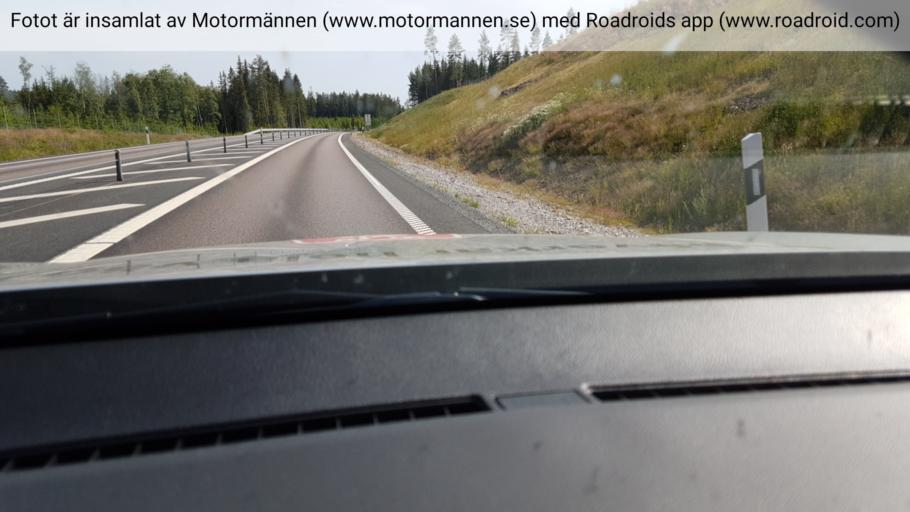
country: SE
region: Joenkoeping
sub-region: Aneby Kommun
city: Aneby
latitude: 57.8329
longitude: 14.8744
